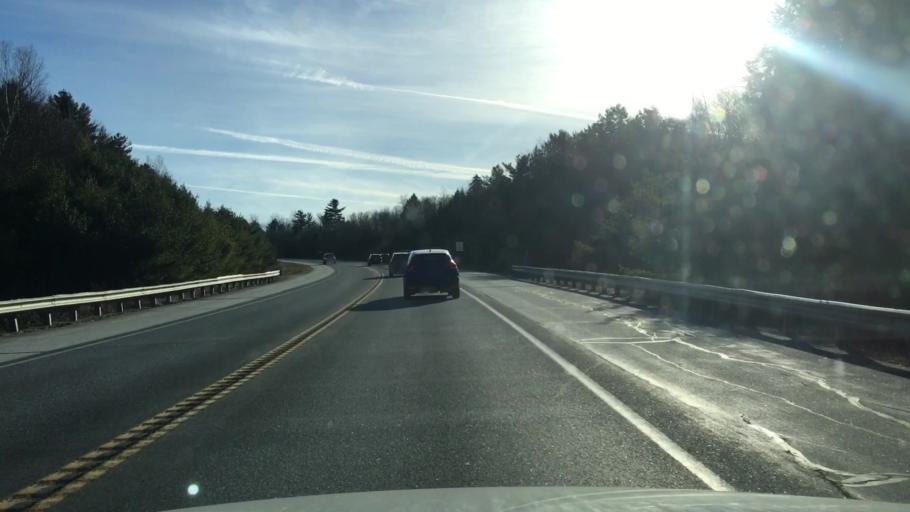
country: US
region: Maine
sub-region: Hancock County
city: Dedham
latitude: 44.6764
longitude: -68.5787
